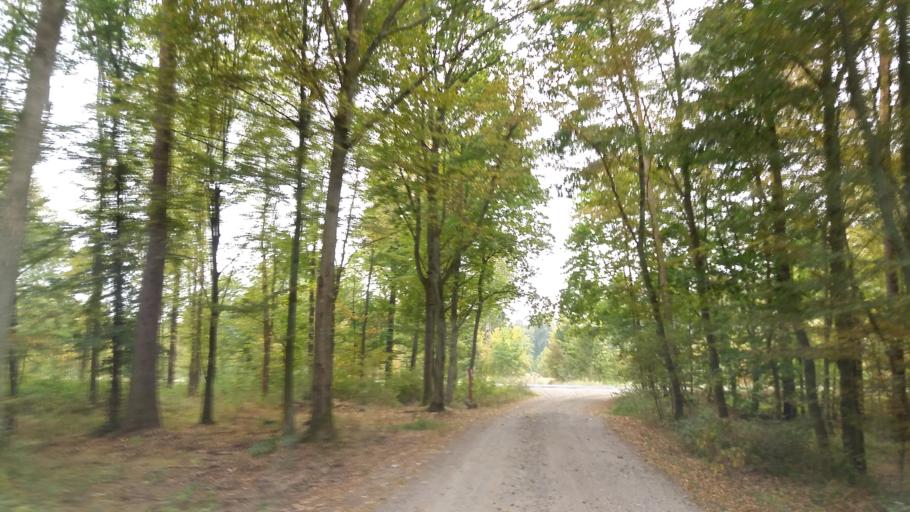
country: PL
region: West Pomeranian Voivodeship
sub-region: Powiat mysliborski
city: Barlinek
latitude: 52.9145
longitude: 15.1949
